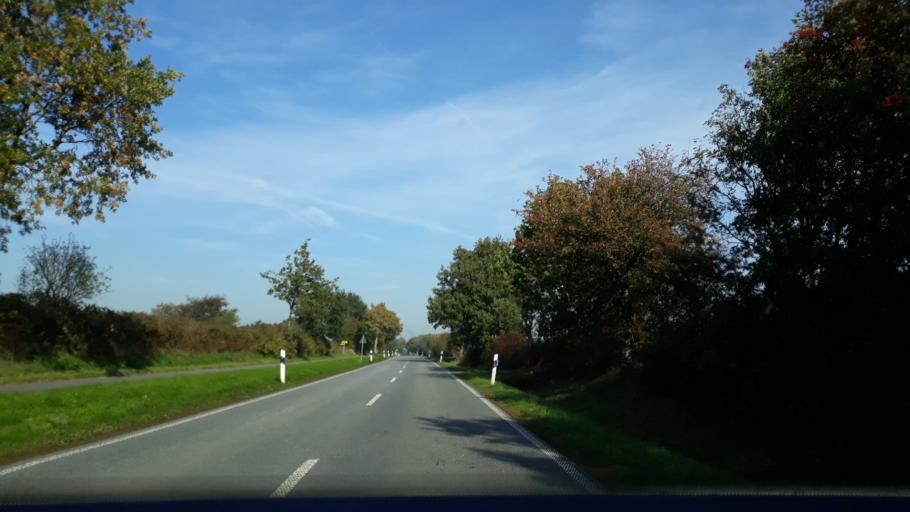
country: DE
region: Schleswig-Holstein
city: Klein Rheide
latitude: 54.4603
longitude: 9.4822
